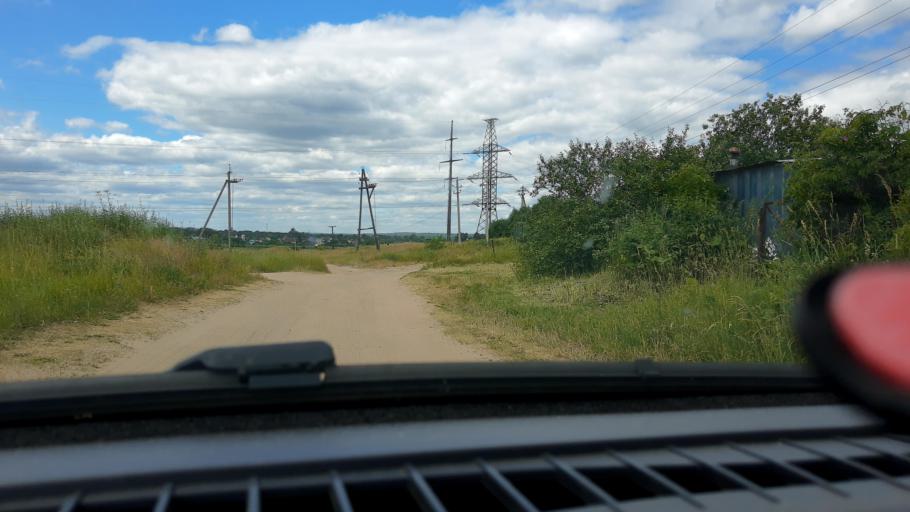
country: RU
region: Nizjnij Novgorod
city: Kstovo
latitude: 56.1415
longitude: 44.1713
